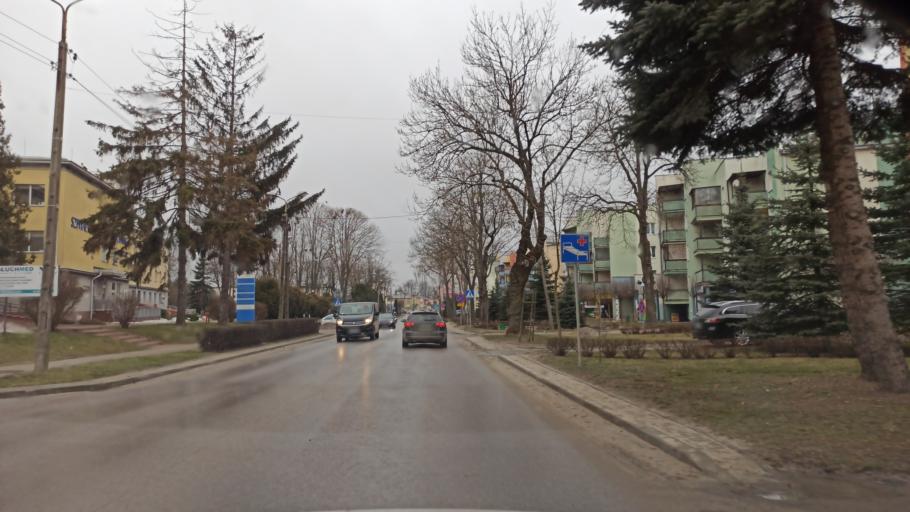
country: PL
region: Lublin Voivodeship
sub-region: Powiat lubelski
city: Bychawa
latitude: 51.0136
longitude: 22.5384
